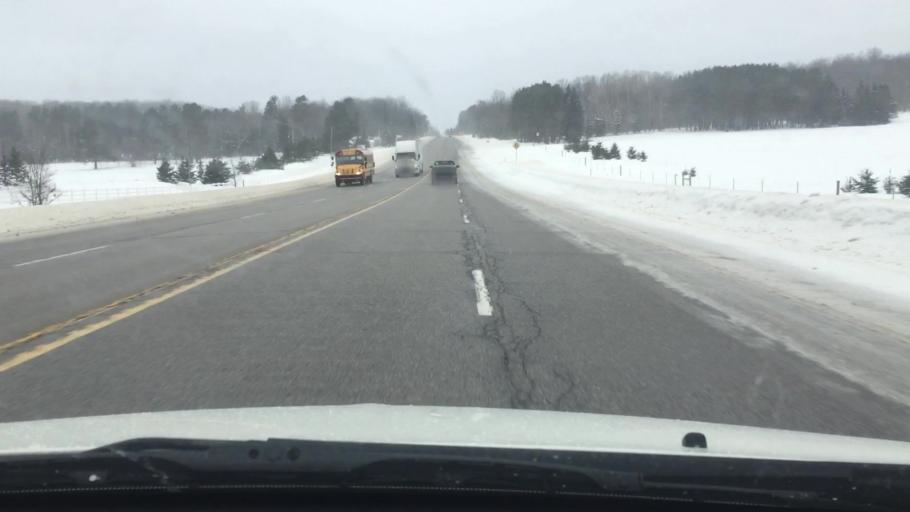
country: US
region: Michigan
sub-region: Otsego County
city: Gaylord
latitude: 45.0510
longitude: -84.7759
